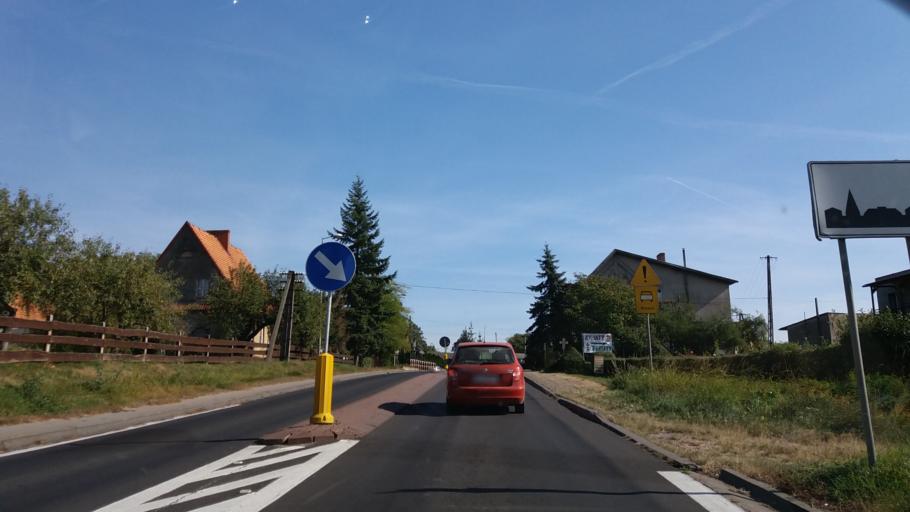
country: PL
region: Greater Poland Voivodeship
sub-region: Powiat miedzychodzki
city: Miedzychod
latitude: 52.5657
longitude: 15.9551
